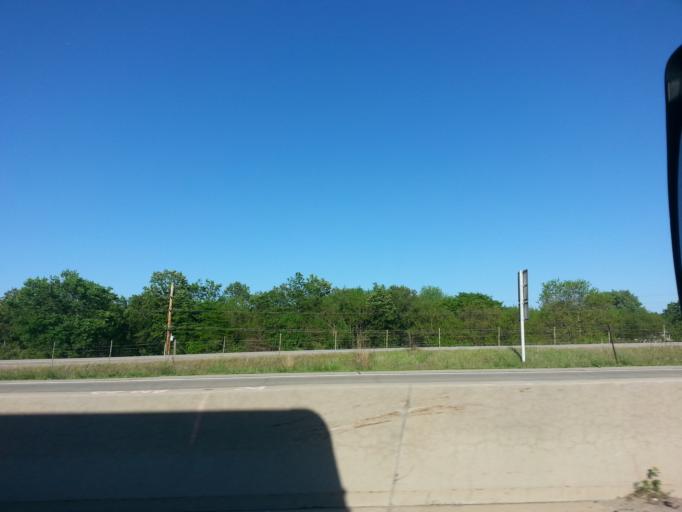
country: US
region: Illinois
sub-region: McLean County
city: Hudson
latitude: 40.6599
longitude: -89.0048
